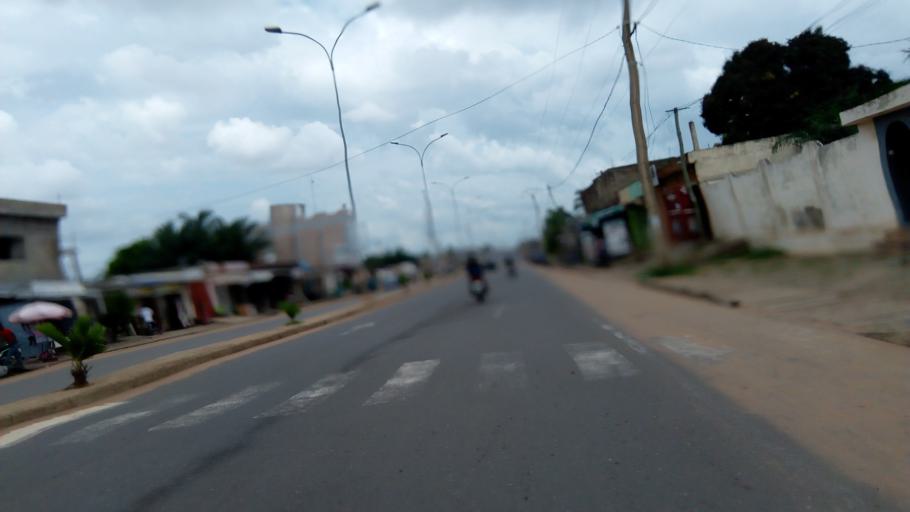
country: TG
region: Maritime
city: Lome
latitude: 6.2091
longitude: 1.1801
